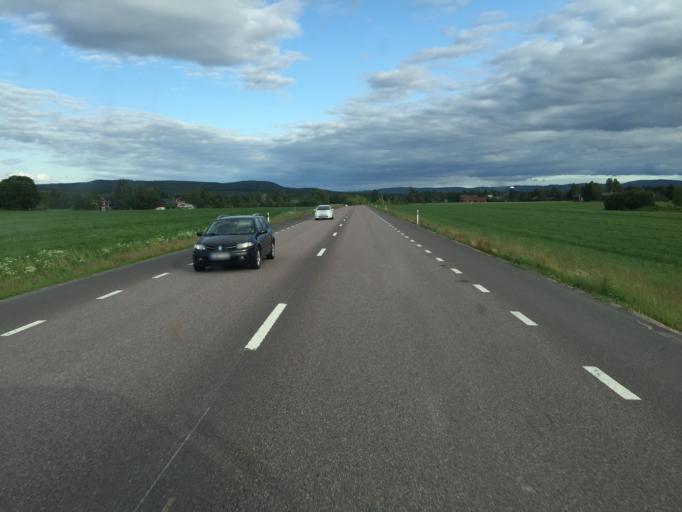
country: SE
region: Dalarna
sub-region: Gagnefs Kommun
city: Gagnef
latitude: 60.5877
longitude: 15.0919
